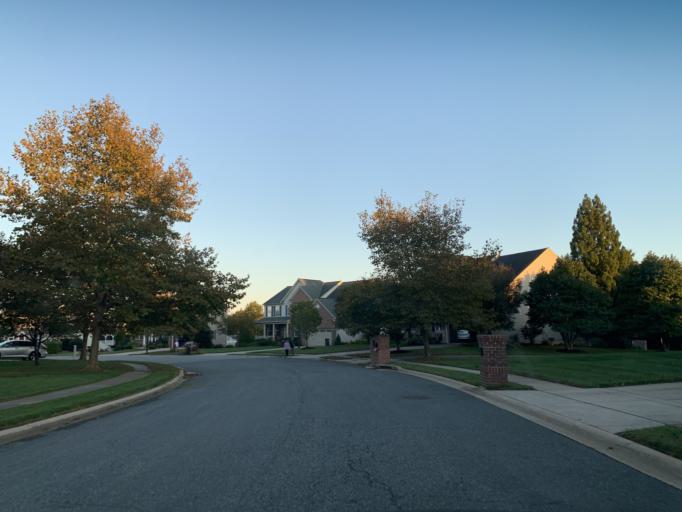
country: US
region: Maryland
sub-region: Harford County
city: Bel Air South
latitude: 39.5280
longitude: -76.3008
